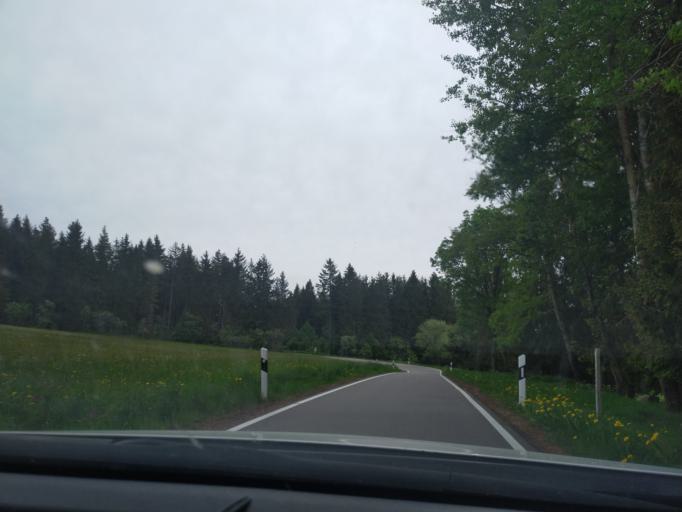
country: DE
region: Baden-Wuerttemberg
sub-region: Freiburg Region
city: Schluchsee
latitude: 47.8067
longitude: 8.2204
